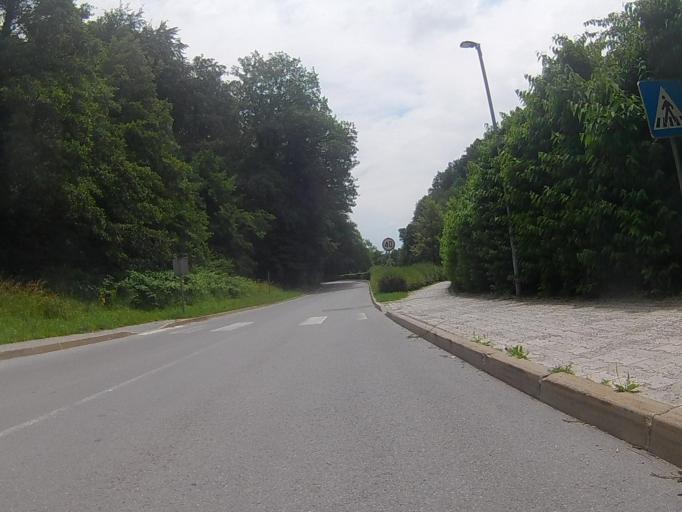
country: SI
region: Maribor
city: Maribor
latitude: 46.5725
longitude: 15.6461
